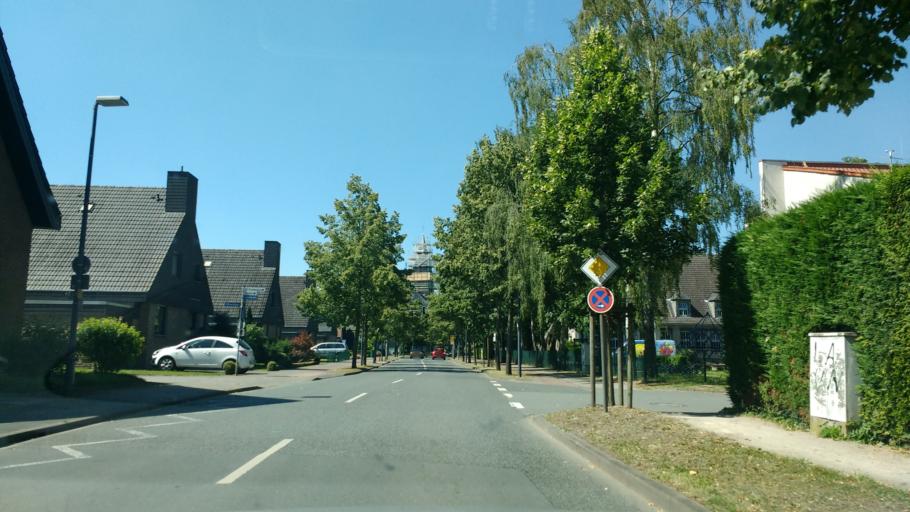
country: DE
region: North Rhine-Westphalia
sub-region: Regierungsbezirk Arnsberg
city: Lippstadt
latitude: 51.6929
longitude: 8.3797
